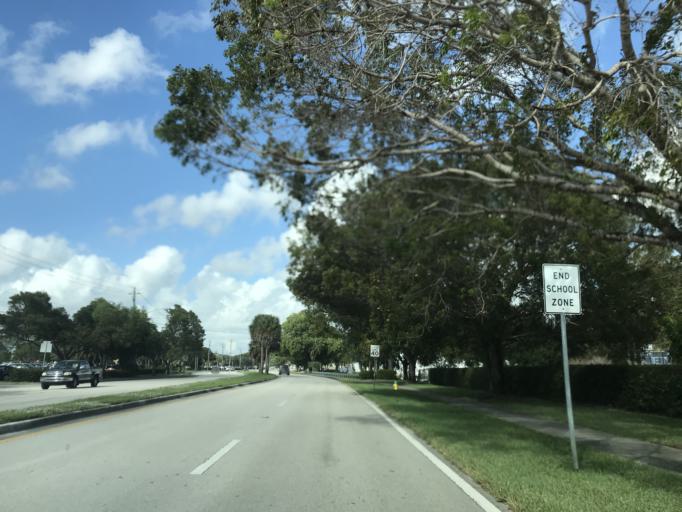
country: US
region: Florida
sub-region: Broward County
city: Margate
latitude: 26.2492
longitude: -80.1942
